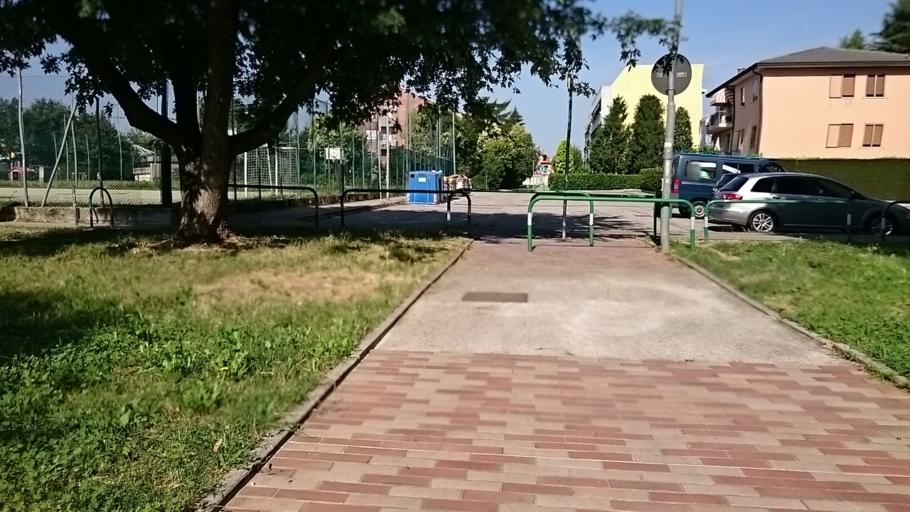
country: IT
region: Veneto
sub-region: Provincia di Padova
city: Mandriola-Sant'Agostino
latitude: 45.3832
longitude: 11.8740
